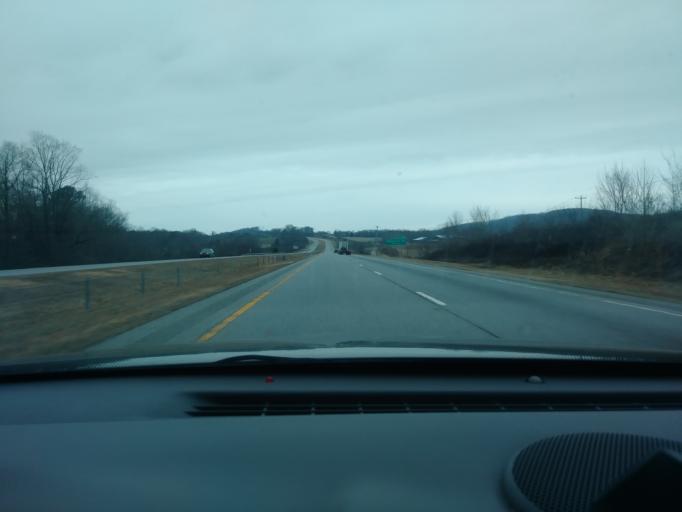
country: US
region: North Carolina
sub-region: Yadkin County
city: Jonesville
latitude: 36.1363
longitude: -80.8584
